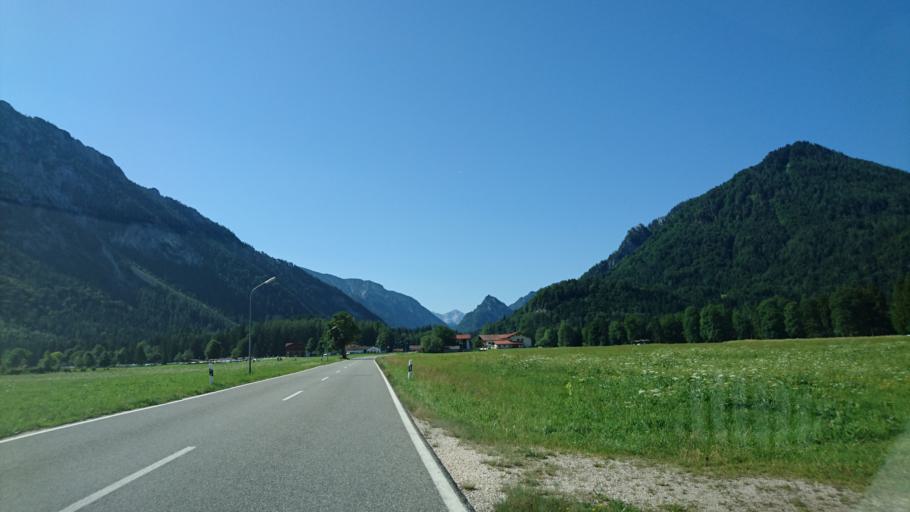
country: DE
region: Bavaria
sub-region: Upper Bavaria
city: Ruhpolding
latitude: 47.7473
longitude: 12.6629
